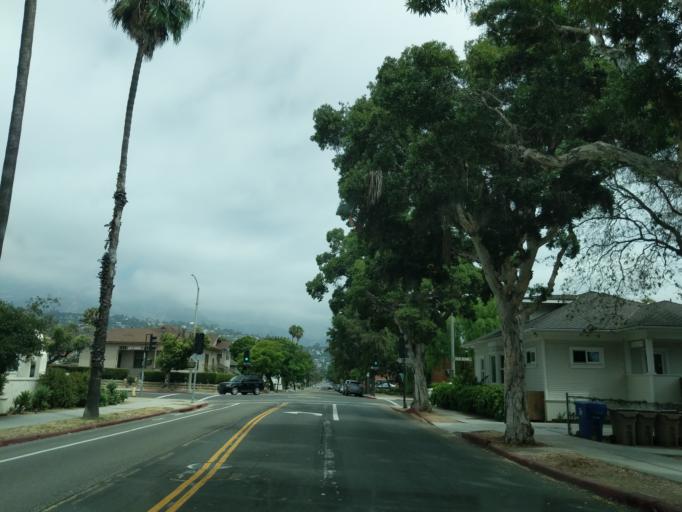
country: US
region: California
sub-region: Santa Barbara County
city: Santa Barbara
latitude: 34.4195
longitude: -119.6949
